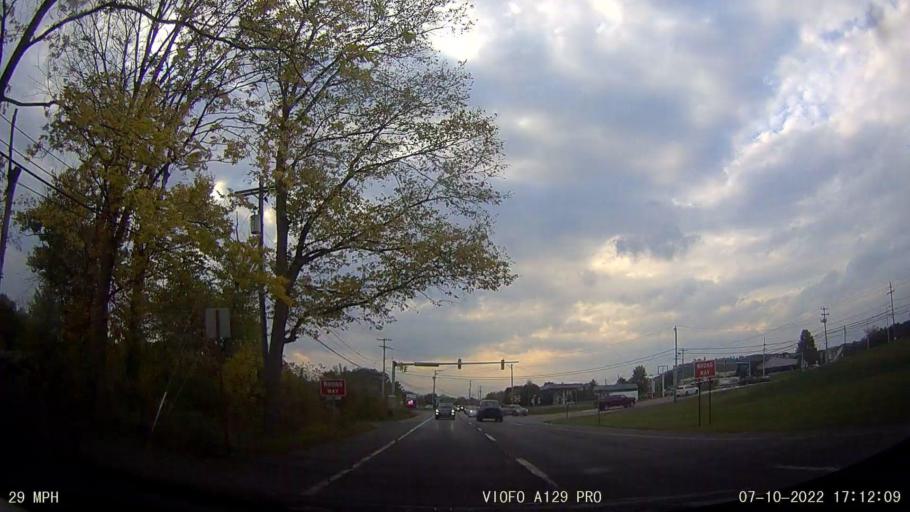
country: US
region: Pennsylvania
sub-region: Berks County
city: Amity Gardens
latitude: 40.2634
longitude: -75.7424
